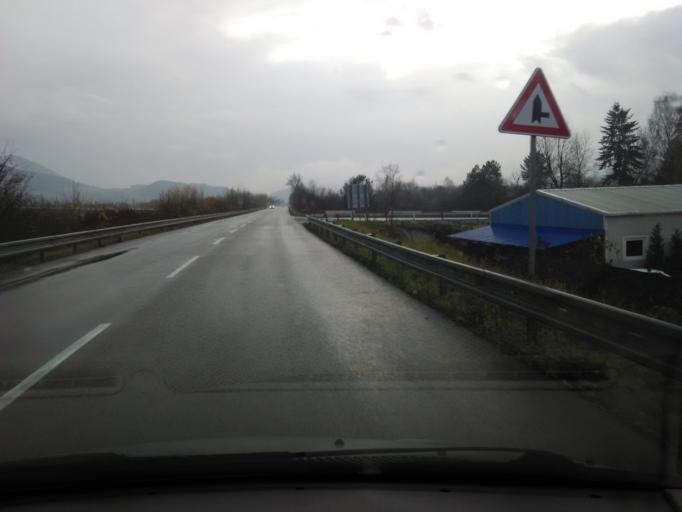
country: SK
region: Zilinsky
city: Bytca
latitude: 49.1909
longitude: 18.5113
